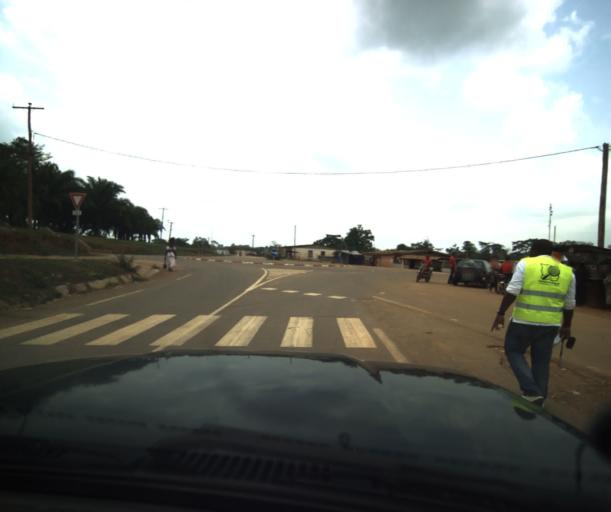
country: CM
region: Centre
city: Akono
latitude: 3.5011
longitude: 11.3281
